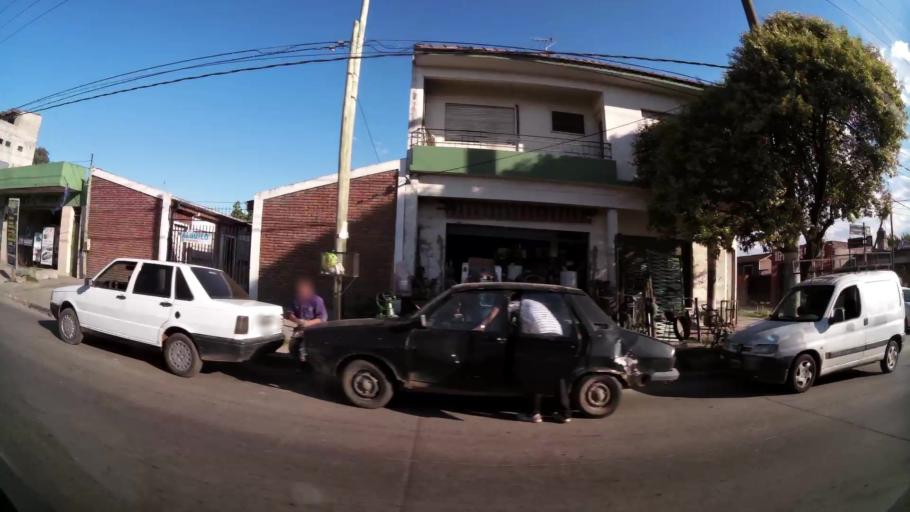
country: AR
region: Buenos Aires
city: Hurlingham
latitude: -34.5060
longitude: -58.7212
